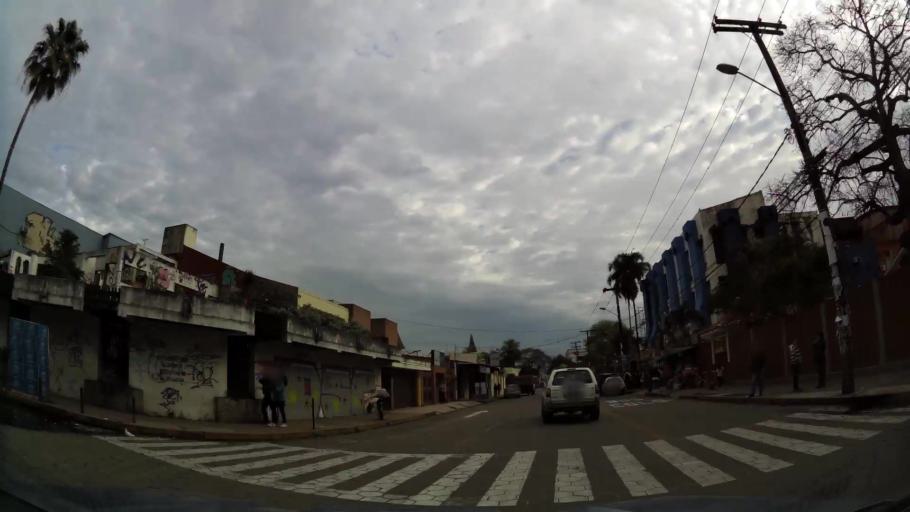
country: BO
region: Santa Cruz
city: Santa Cruz de la Sierra
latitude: -17.7903
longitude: -63.1781
